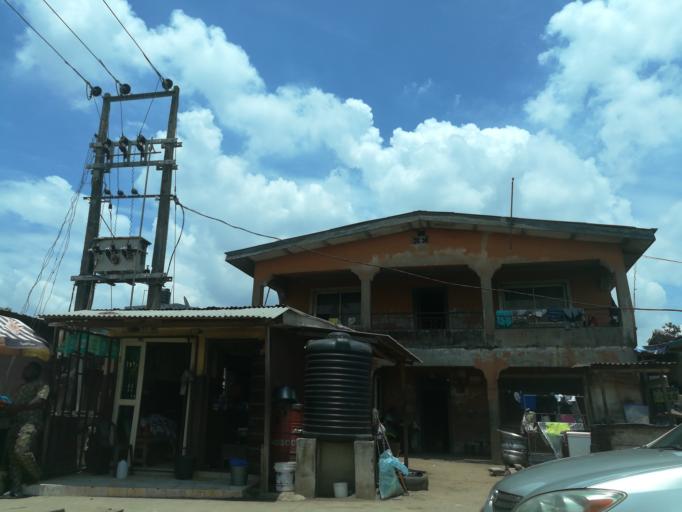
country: NG
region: Lagos
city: Ebute Ikorodu
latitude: 6.6026
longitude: 3.4906
